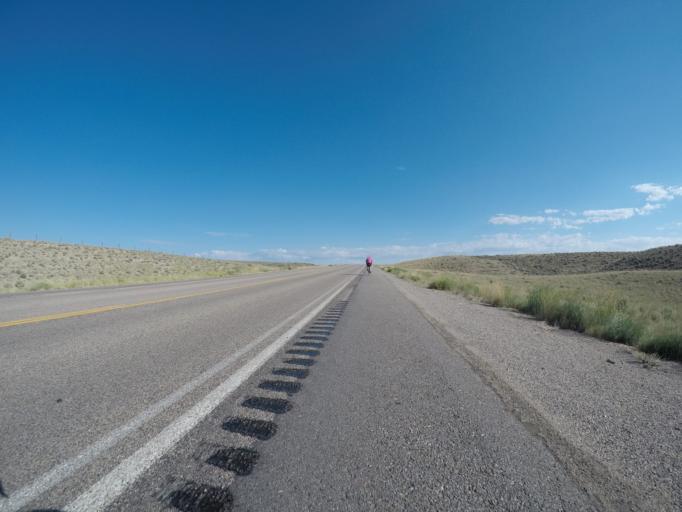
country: US
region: Wyoming
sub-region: Lincoln County
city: Kemmerer
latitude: 42.0477
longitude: -110.1610
